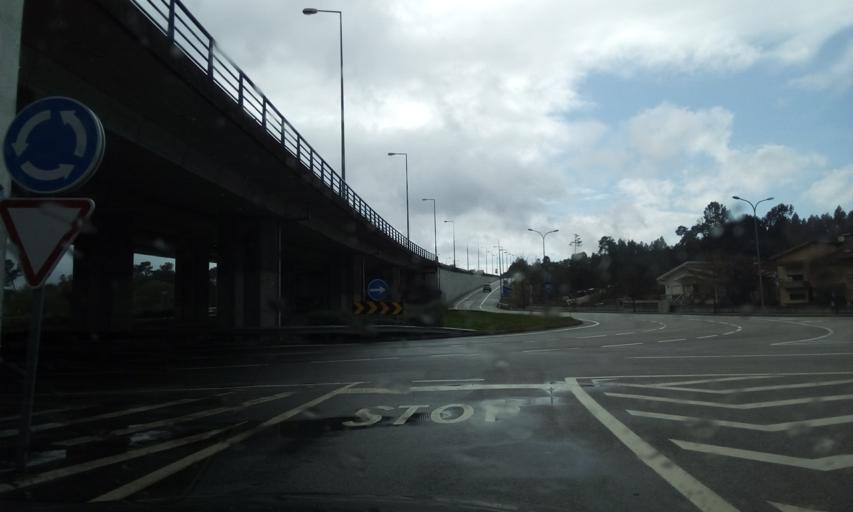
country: PT
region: Viseu
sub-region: Viseu
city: Viseu
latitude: 40.6225
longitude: -7.9181
